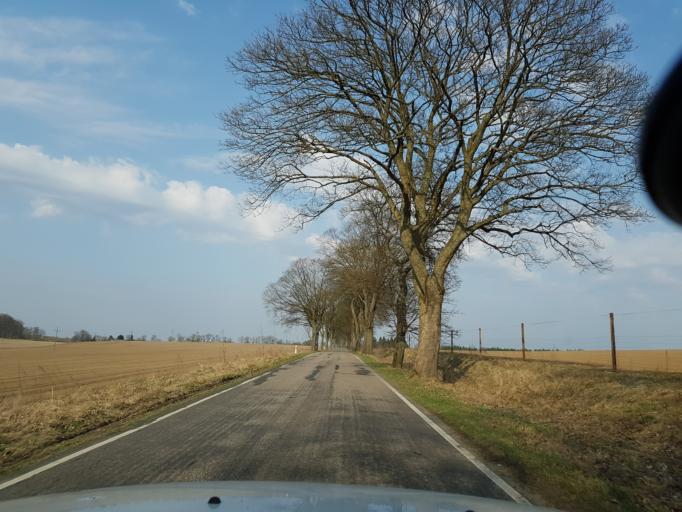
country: PL
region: West Pomeranian Voivodeship
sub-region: Powiat drawski
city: Drawsko Pomorskie
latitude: 53.5932
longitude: 15.8966
